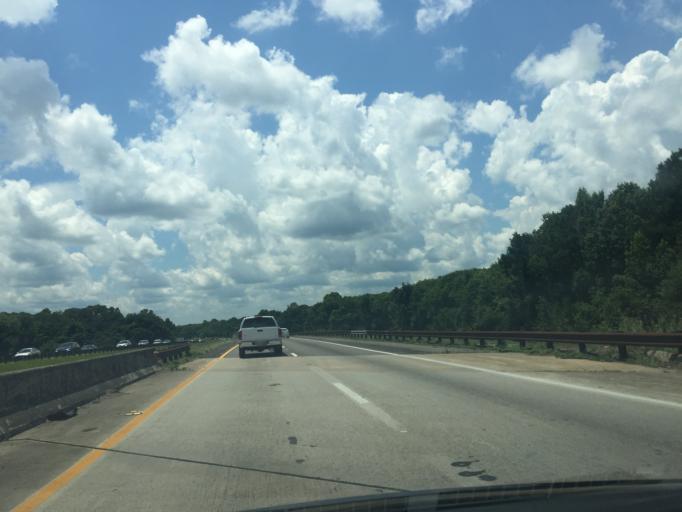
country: US
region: South Carolina
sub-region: Jasper County
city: Hardeeville
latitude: 32.2541
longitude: -81.1151
